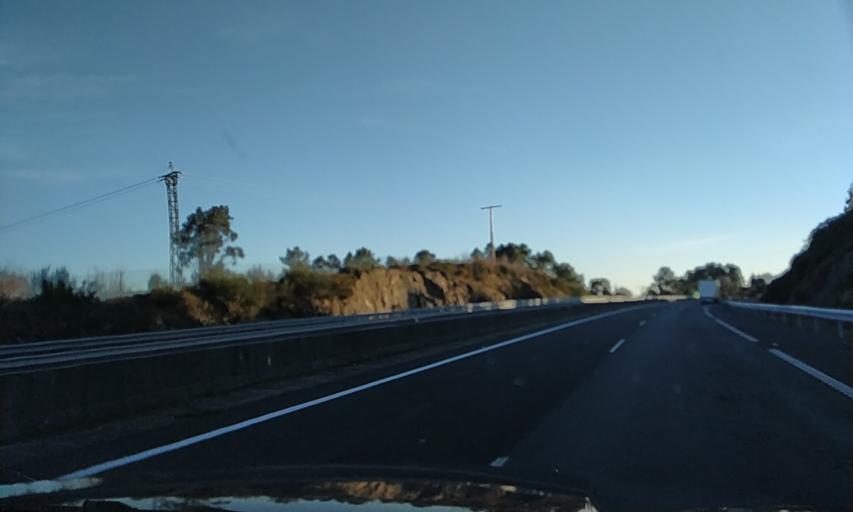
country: ES
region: Galicia
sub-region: Provincia de Ourense
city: Pinor
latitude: 42.5069
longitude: -8.0233
